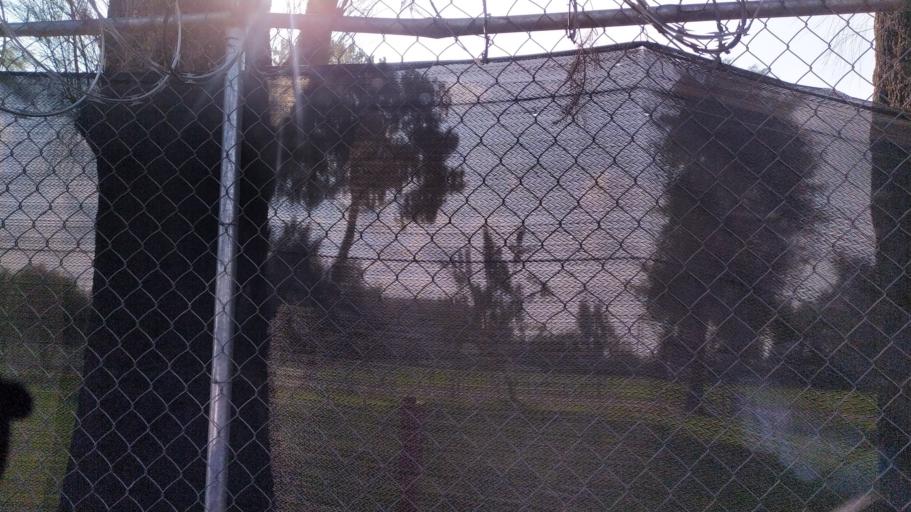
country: MX
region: Jalisco
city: Zapopan2
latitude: 20.6947
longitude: -103.4475
